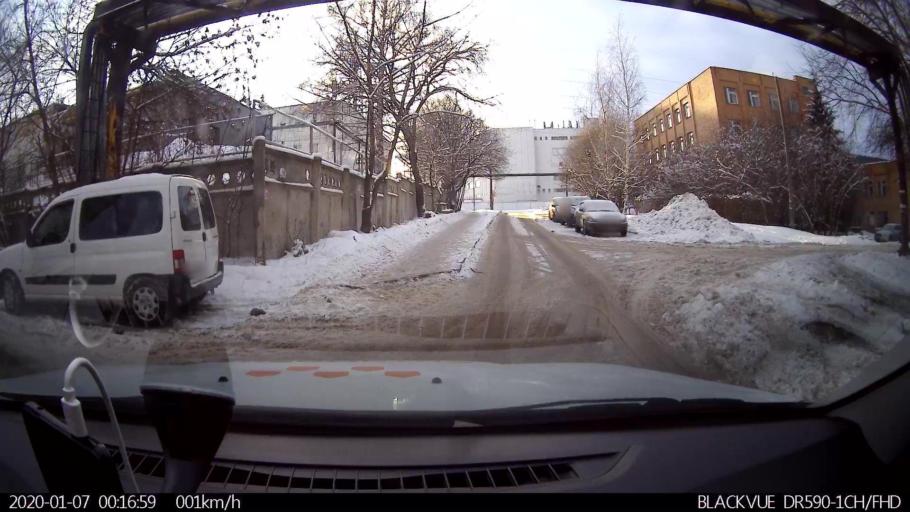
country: RU
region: Nizjnij Novgorod
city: Nizhniy Novgorod
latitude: 56.2348
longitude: 43.9445
